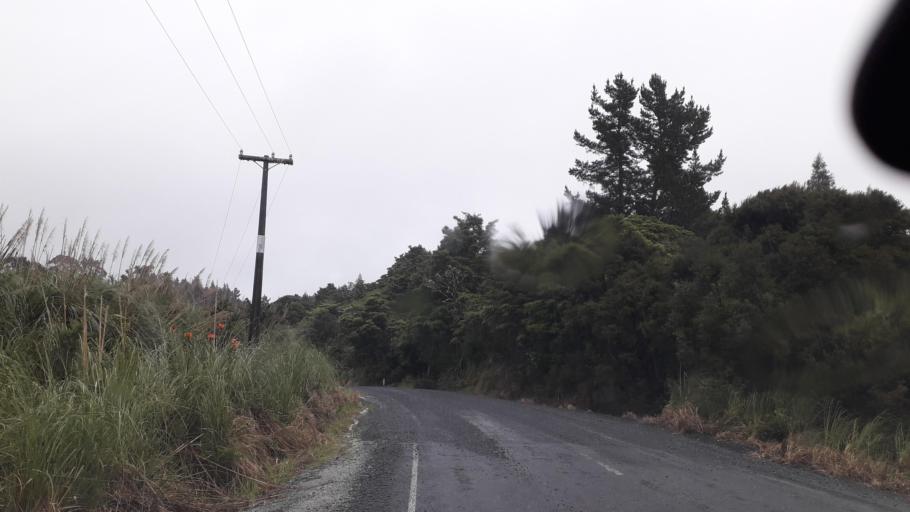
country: NZ
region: Northland
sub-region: Far North District
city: Kerikeri
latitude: -35.1155
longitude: 173.7538
